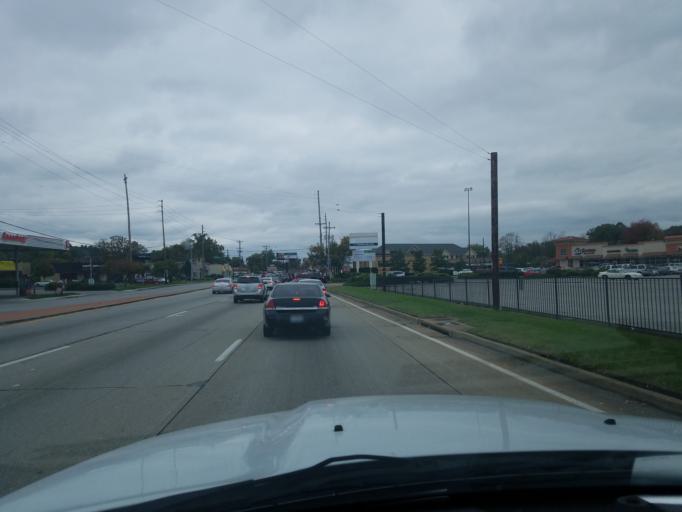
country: US
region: Kentucky
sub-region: Jefferson County
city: Shively
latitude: 38.1822
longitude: -85.8153
